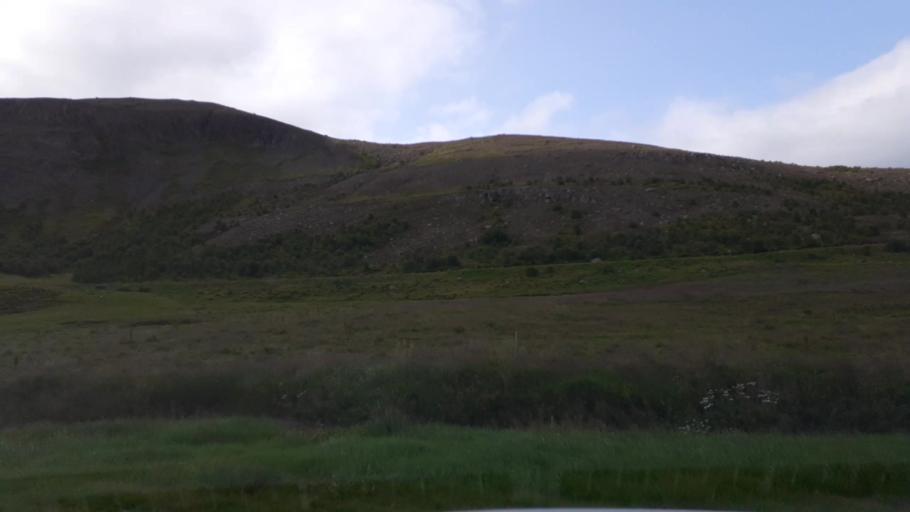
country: IS
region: Northeast
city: Akureyri
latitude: 65.9448
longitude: -18.1877
